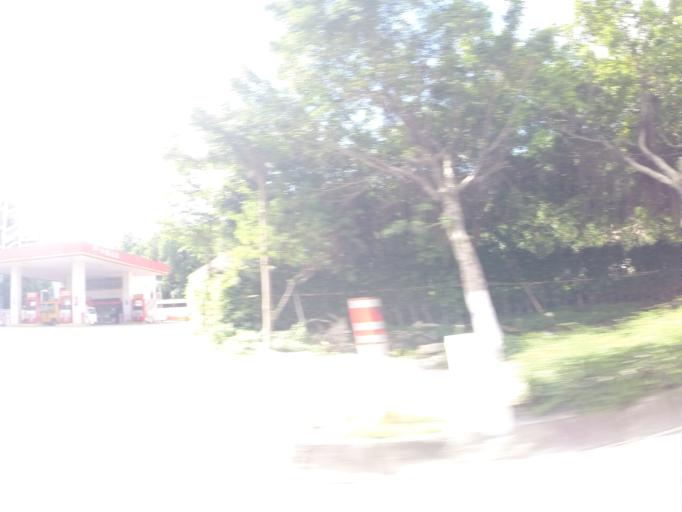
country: CN
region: Guangdong
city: Tangjiawan
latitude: 22.3184
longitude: 113.5962
